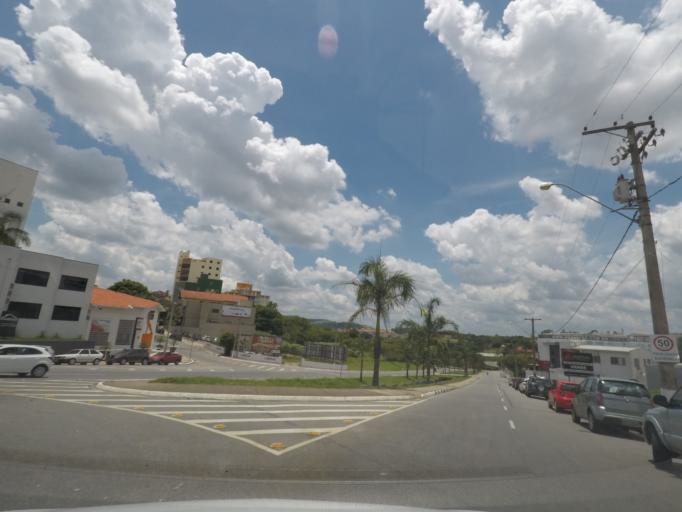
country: BR
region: Sao Paulo
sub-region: Vinhedo
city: Vinhedo
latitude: -23.0390
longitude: -46.9837
